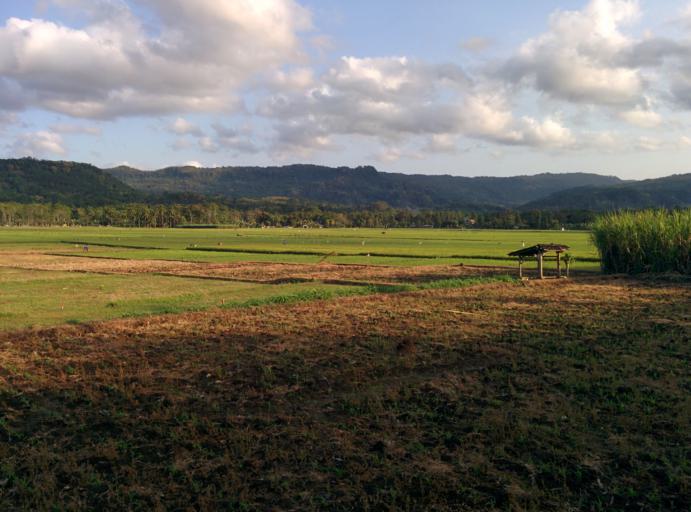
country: ID
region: East Java
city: Sitiarjo
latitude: -8.3844
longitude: 112.6783
